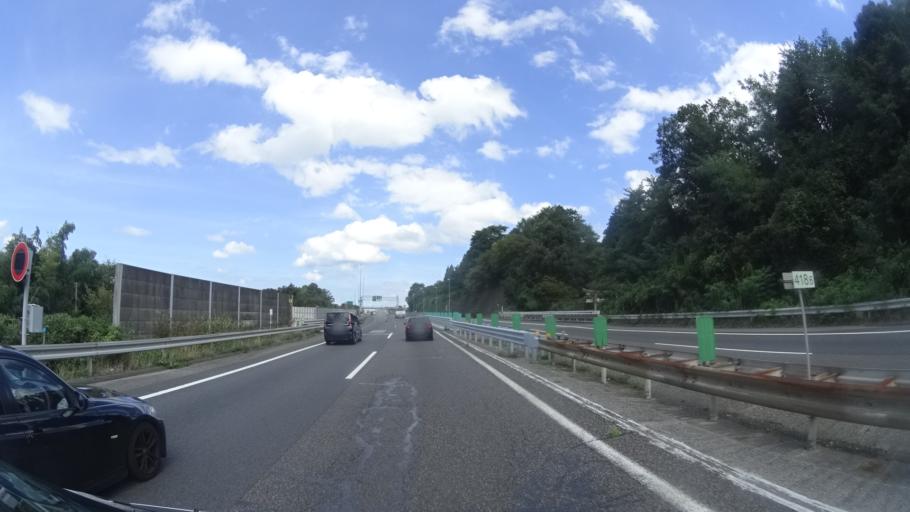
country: JP
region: Shiga Prefecture
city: Hikone
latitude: 35.2133
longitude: 136.2863
